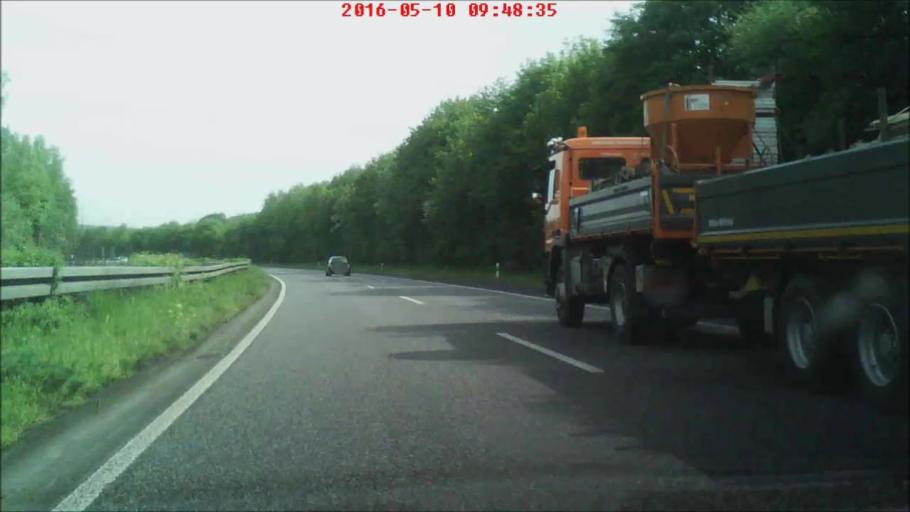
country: DE
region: Hesse
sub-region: Regierungsbezirk Darmstadt
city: Gelnhausen
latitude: 50.2002
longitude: 9.2232
